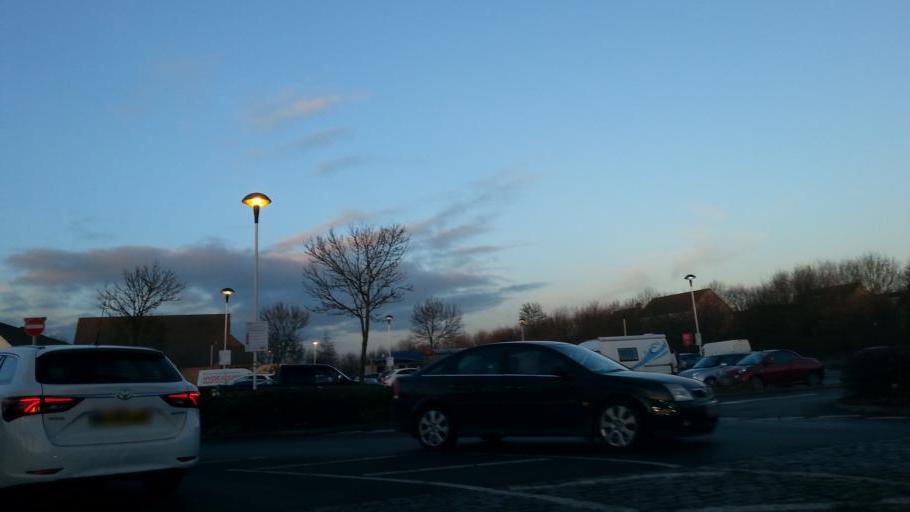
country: GB
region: England
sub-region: Cambridgeshire
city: Huntingdon
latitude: 52.3517
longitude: -0.1794
